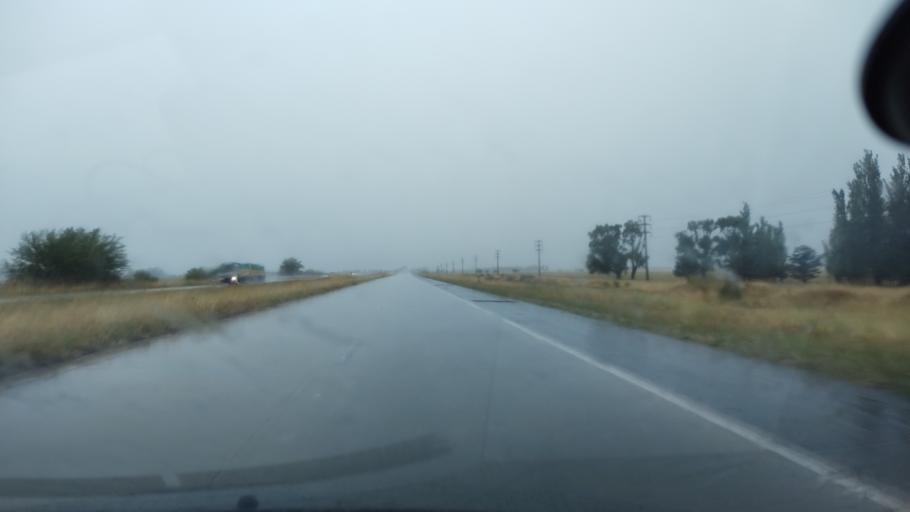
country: AR
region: Buenos Aires
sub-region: Partido de San Vicente
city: San Vicente
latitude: -35.0741
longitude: -58.5435
